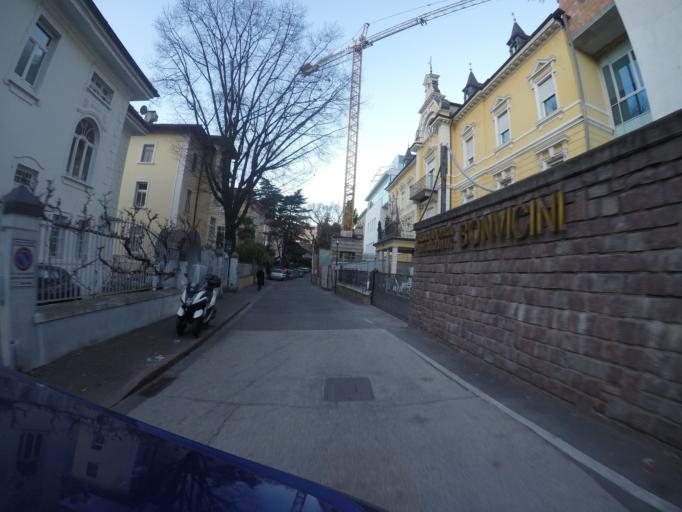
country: IT
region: Trentino-Alto Adige
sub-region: Bolzano
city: Bolzano
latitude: 46.5063
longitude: 11.3347
